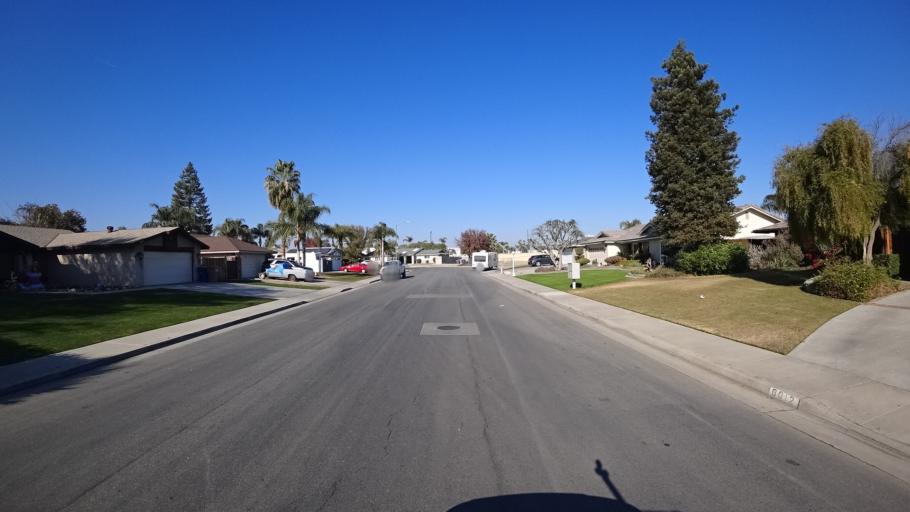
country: US
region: California
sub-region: Kern County
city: Greenfield
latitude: 35.2987
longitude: -119.0365
